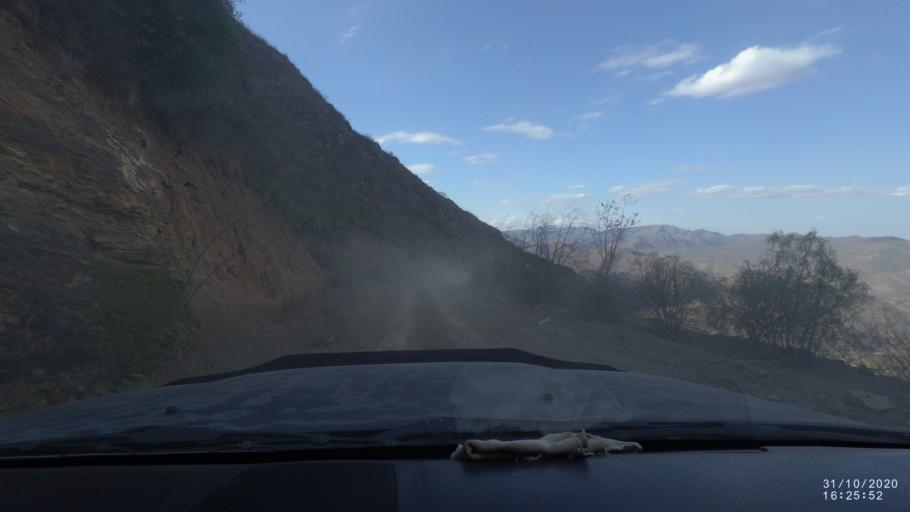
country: BO
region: Chuquisaca
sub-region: Provincia Zudanez
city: Mojocoya
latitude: -18.3979
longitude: -64.5870
